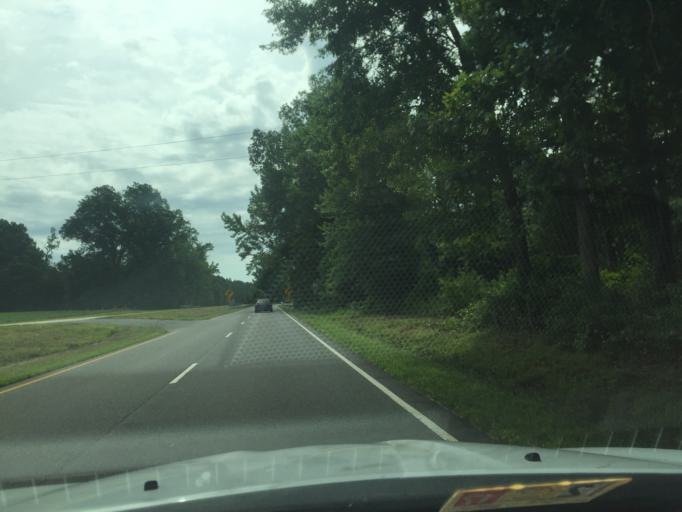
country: US
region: Virginia
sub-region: Charles City County
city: Charles City
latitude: 37.4546
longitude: -77.0830
